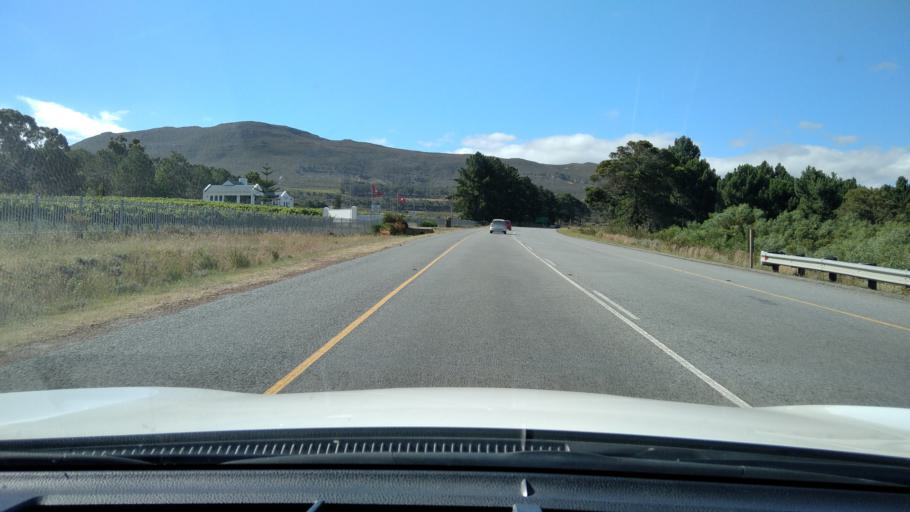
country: ZA
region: Western Cape
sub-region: Overberg District Municipality
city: Hermanus
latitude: -34.3043
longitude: 19.1444
